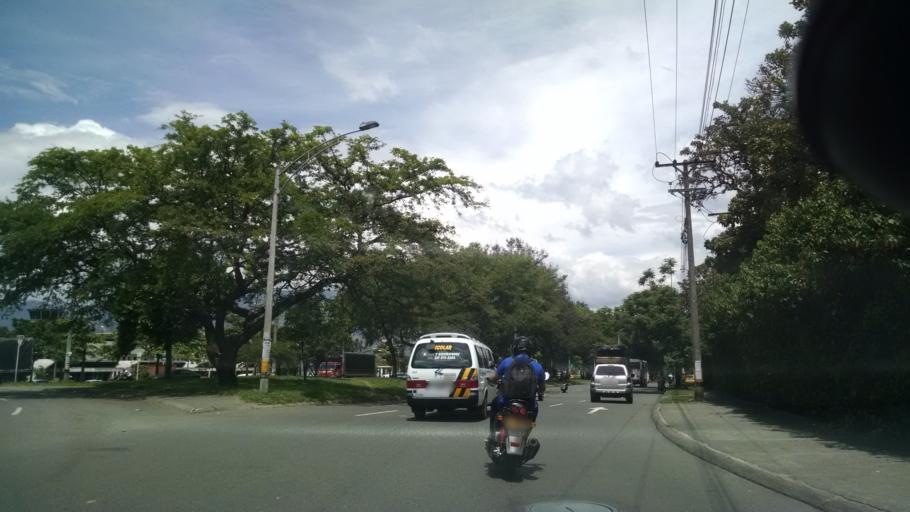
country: CO
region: Antioquia
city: Itagui
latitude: 6.2172
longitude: -75.5857
